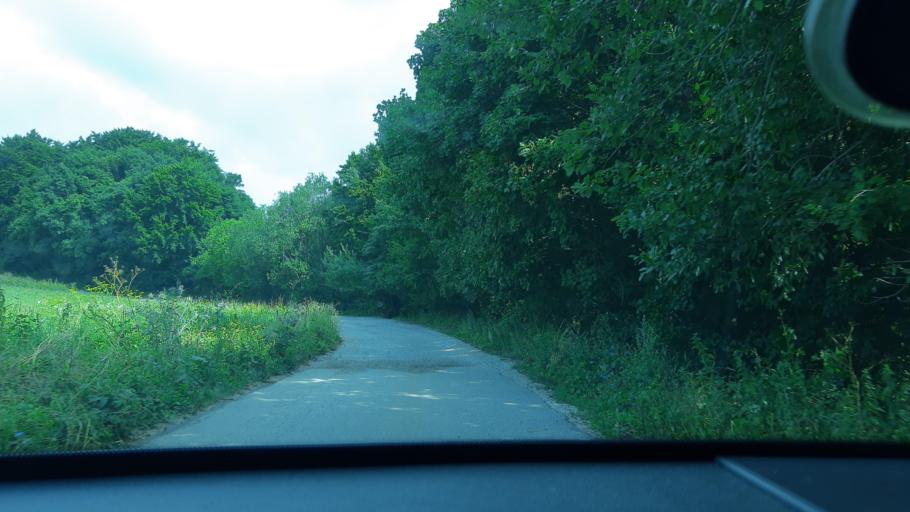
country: SK
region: Trnavsky
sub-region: Okres Trnava
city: Piestany
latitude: 48.6601
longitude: 17.9689
